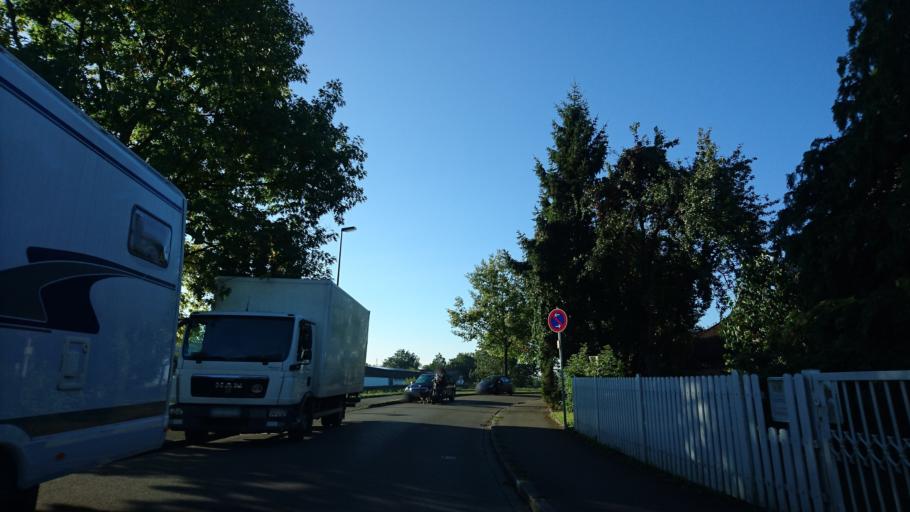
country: DE
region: Bavaria
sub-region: Swabia
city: Gersthofen
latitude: 48.4220
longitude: 10.8875
